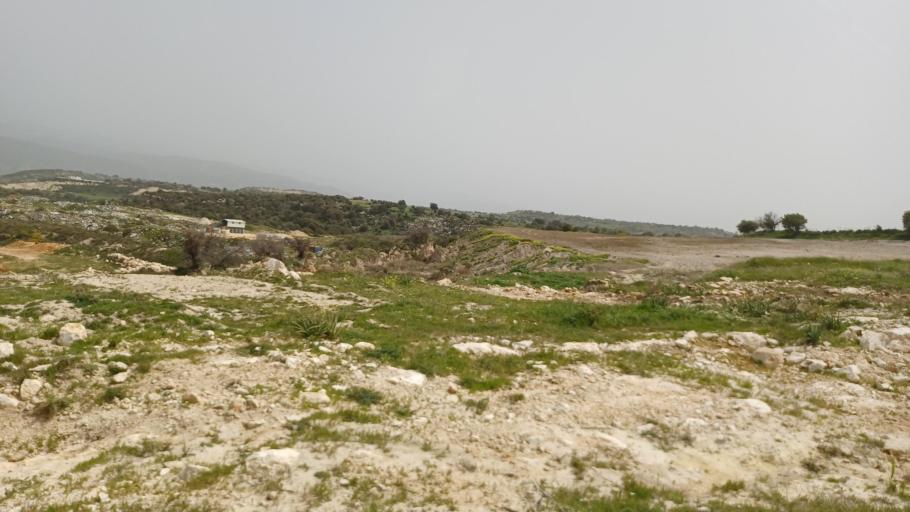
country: CY
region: Pafos
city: Polis
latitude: 34.9946
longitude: 32.3897
